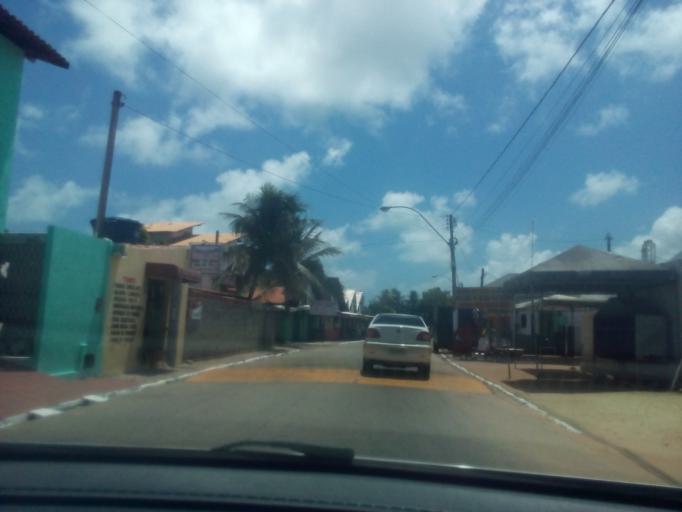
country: BR
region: Rio Grande do Norte
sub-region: Parnamirim
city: Parnamirim
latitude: -5.9705
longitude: -35.1354
